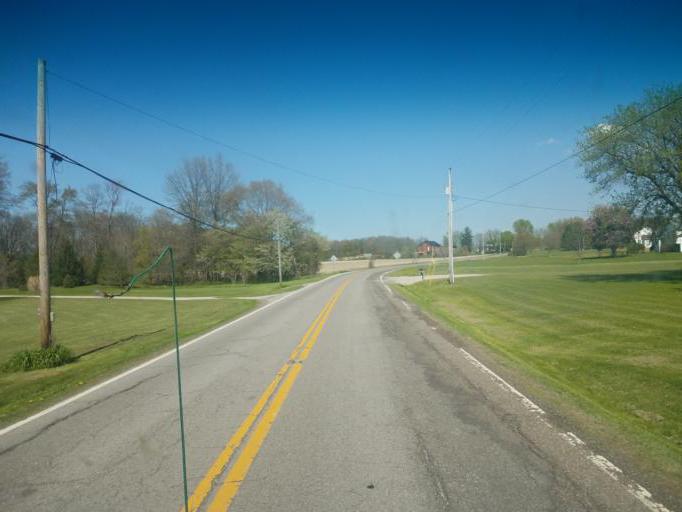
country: US
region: Ohio
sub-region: Wayne County
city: West Salem
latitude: 40.9186
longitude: -82.1065
